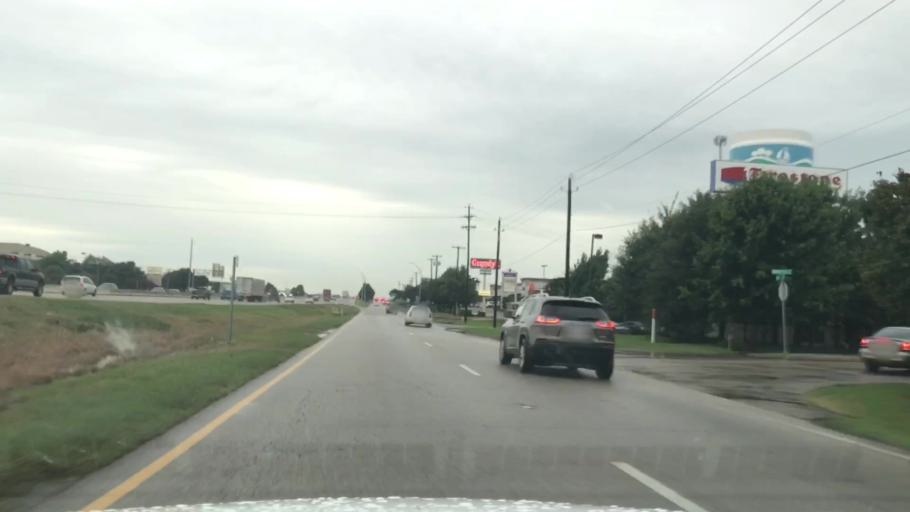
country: US
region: Texas
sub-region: Rockwall County
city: Rockwall
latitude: 32.8996
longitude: -96.4625
